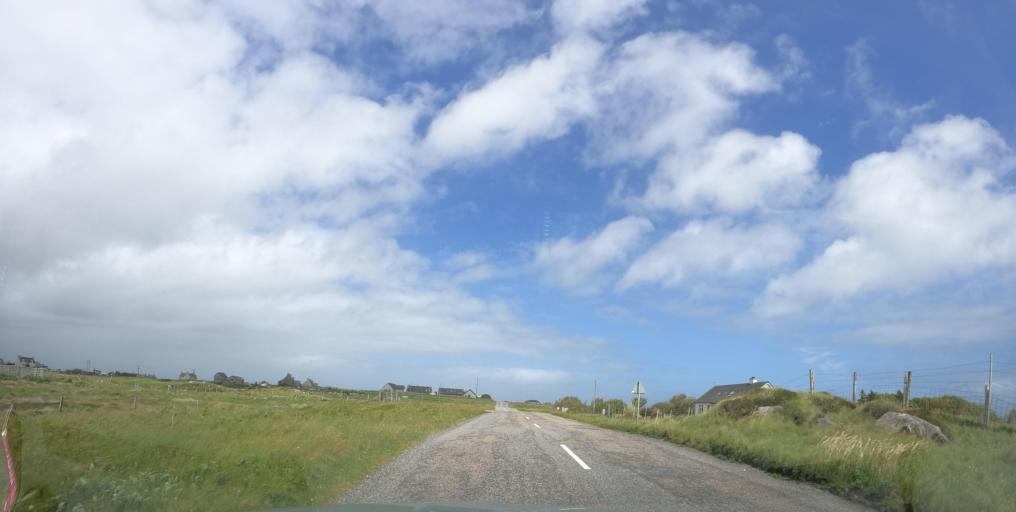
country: GB
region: Scotland
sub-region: Eilean Siar
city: Benbecula
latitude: 57.3502
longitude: -7.3579
